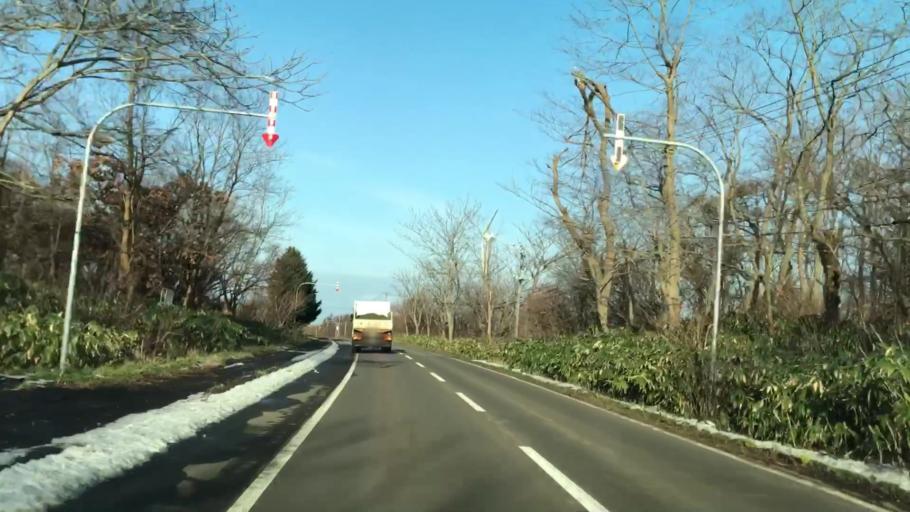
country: JP
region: Hokkaido
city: Yoichi
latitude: 43.3361
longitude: 140.4640
